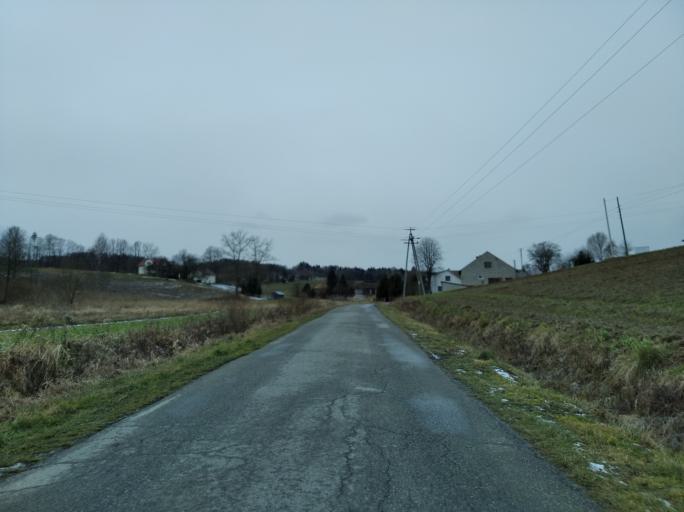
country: PL
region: Subcarpathian Voivodeship
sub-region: Powiat strzyzowski
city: Strzyzow
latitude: 49.9014
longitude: 21.7362
